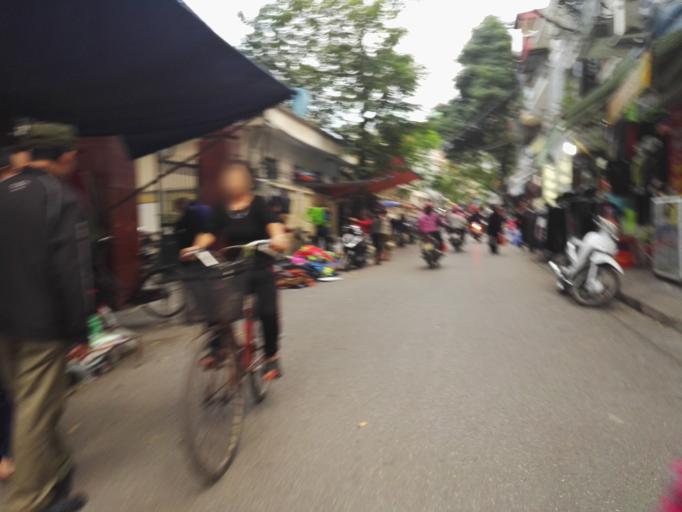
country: VN
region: Ha Noi
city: Hoan Kiem
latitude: 21.0437
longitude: 105.8503
